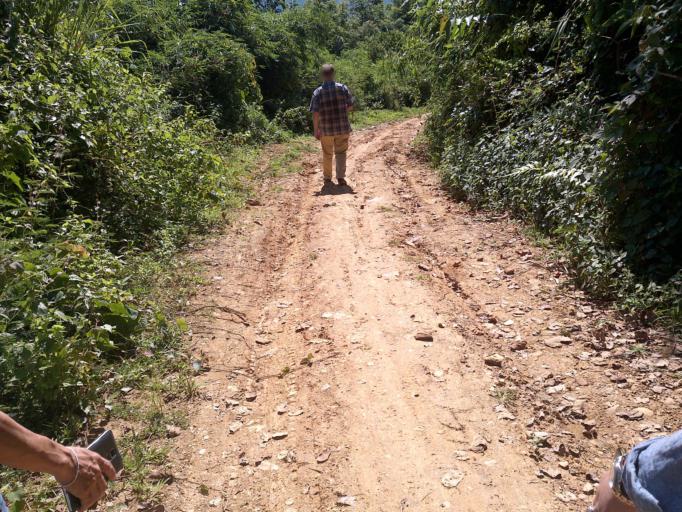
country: TH
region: Nan
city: Chaloem Phra Kiat
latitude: 19.9421
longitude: 101.1650
